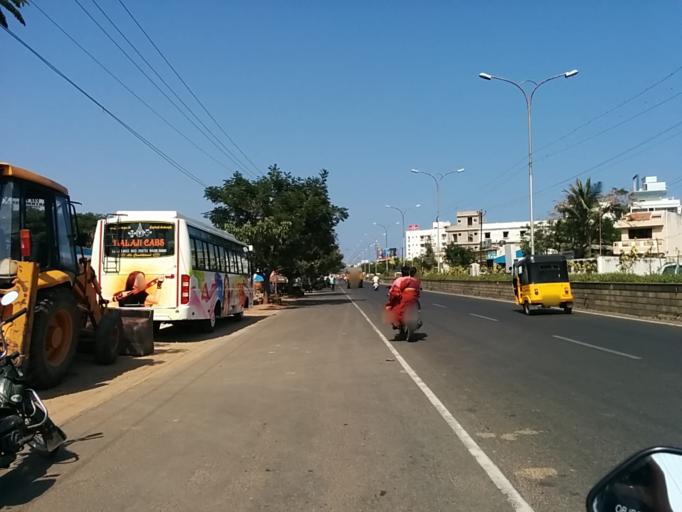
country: IN
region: Pondicherry
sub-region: Puducherry
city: Puducherry
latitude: 11.9457
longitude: 79.8103
